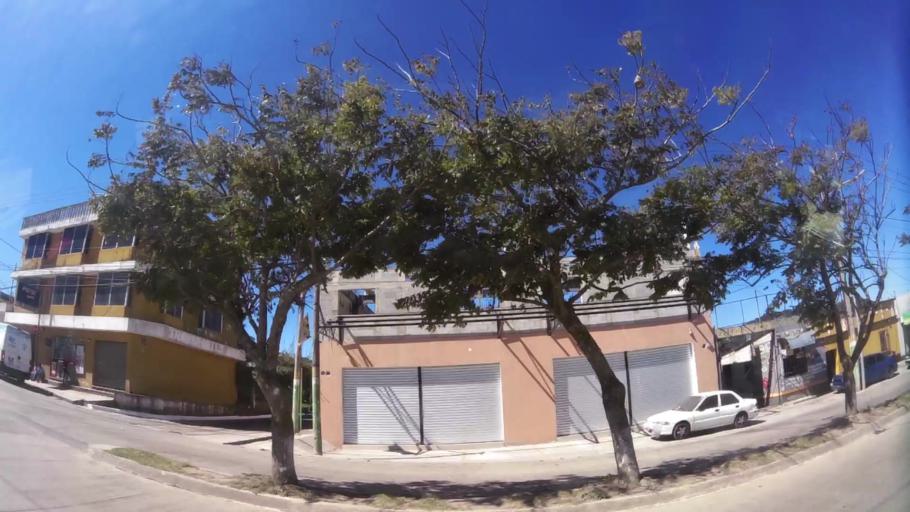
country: GT
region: Guatemala
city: San Jose Pinula
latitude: 14.5439
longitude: -90.4089
